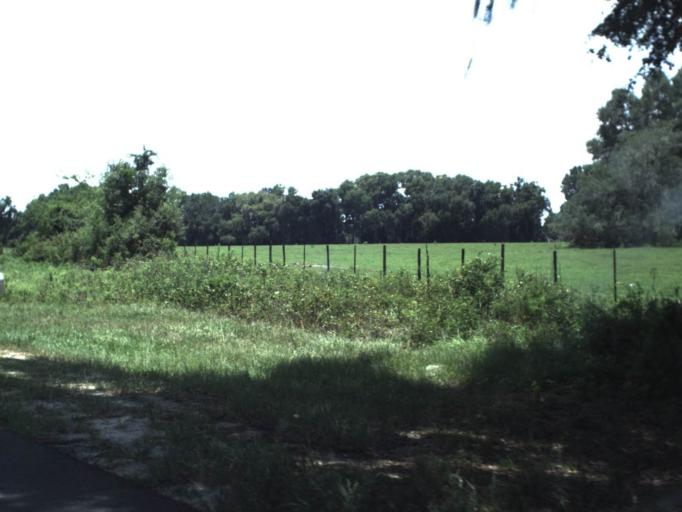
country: US
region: Florida
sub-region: Hamilton County
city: Jasper
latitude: 30.5541
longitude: -82.9810
